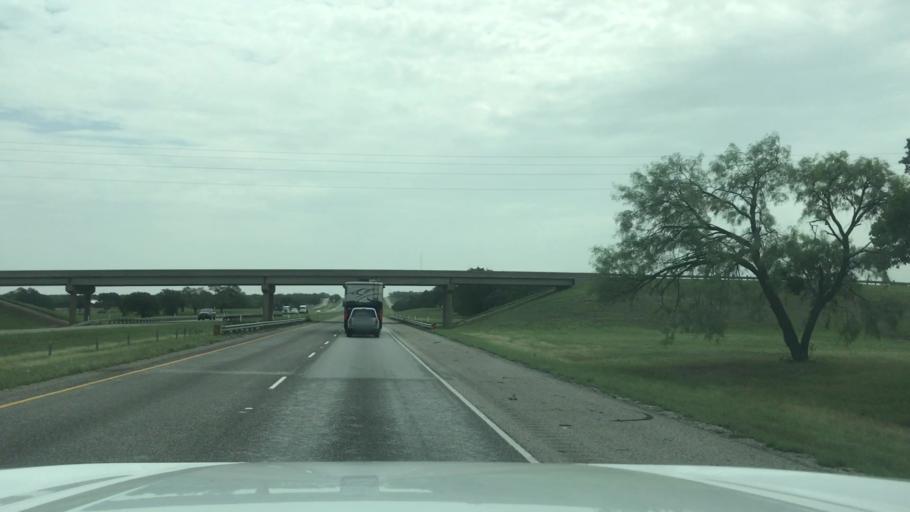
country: US
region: Texas
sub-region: Eastland County
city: Eastland
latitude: 32.3754
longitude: -98.8879
